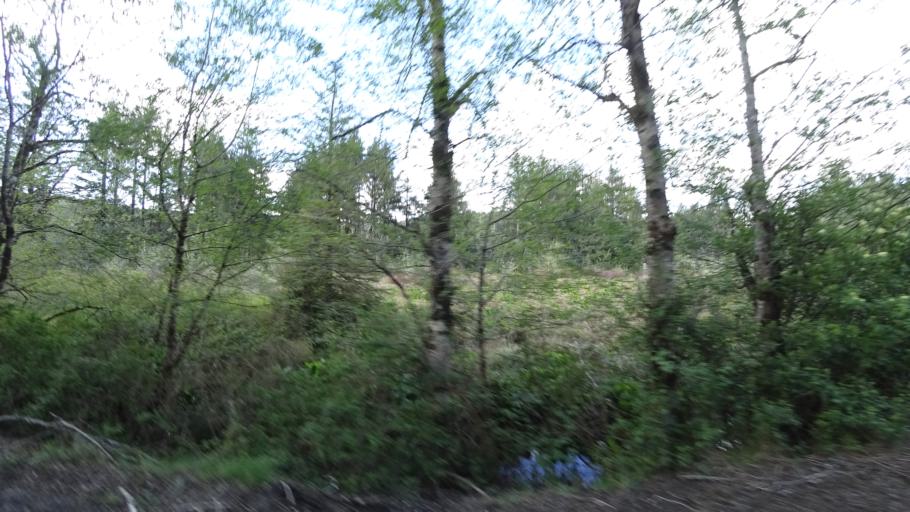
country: US
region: Oregon
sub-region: Douglas County
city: Reedsport
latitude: 43.7551
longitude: -124.1415
